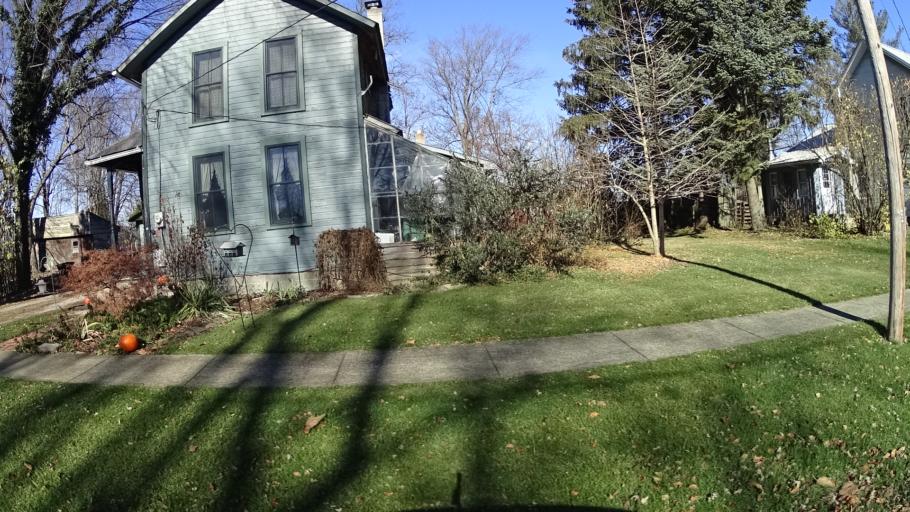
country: US
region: Ohio
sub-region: Lorain County
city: Wellington
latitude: 41.1249
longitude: -82.3031
